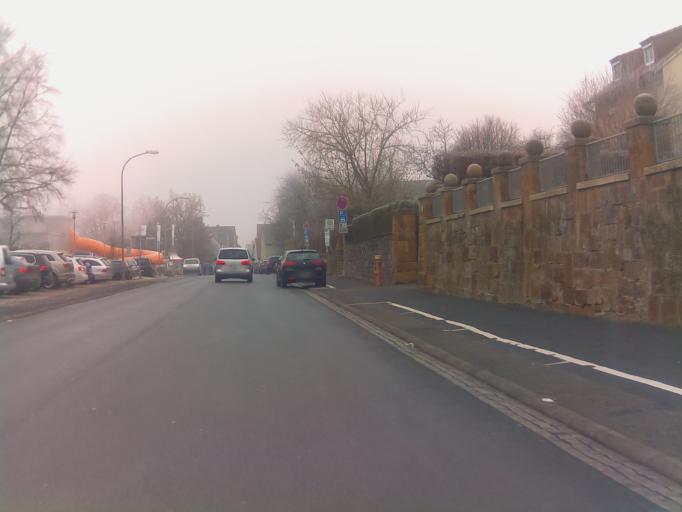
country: DE
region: Bavaria
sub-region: Regierungsbezirk Unterfranken
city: Gerolzhofen
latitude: 49.8996
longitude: 10.3575
